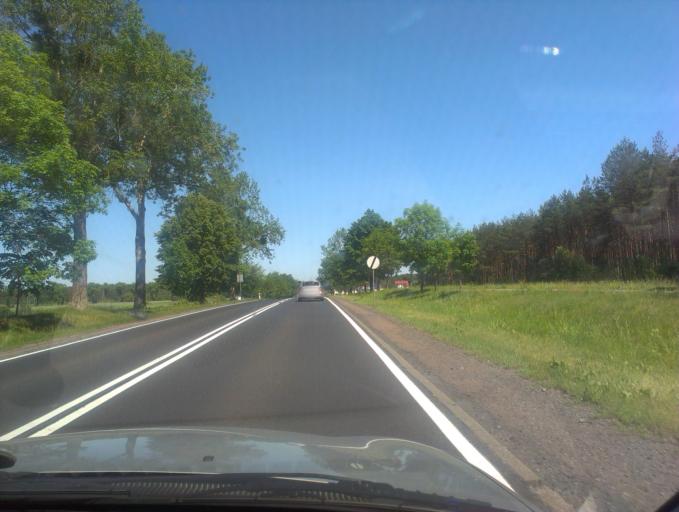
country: PL
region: Pomeranian Voivodeship
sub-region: Powiat czluchowski
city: Czluchow
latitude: 53.6831
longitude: 17.4179
